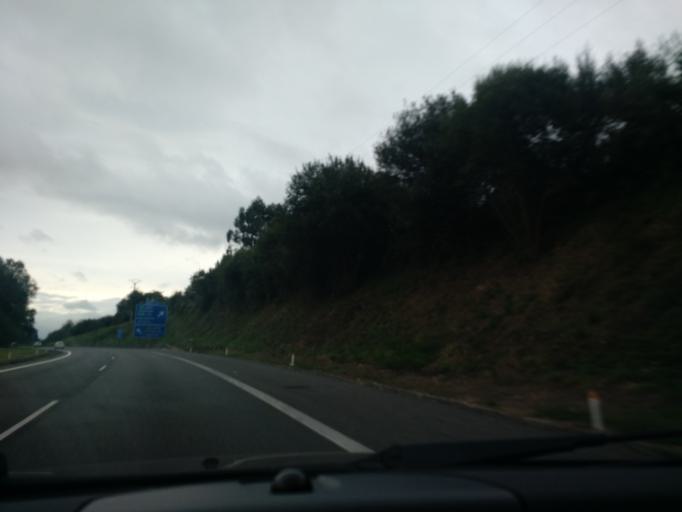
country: ES
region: Galicia
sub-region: Provincia da Coruna
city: Oleiros
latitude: 43.2905
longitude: -8.2955
